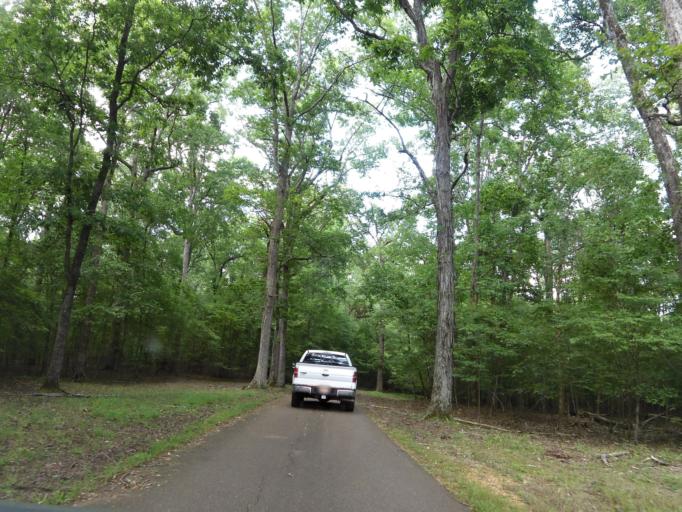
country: US
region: Tennessee
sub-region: Hardin County
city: Crump
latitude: 35.1430
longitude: -88.3217
